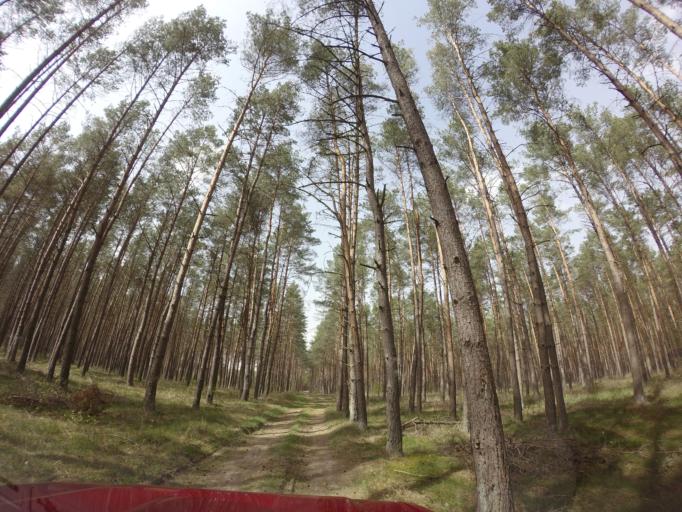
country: PL
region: West Pomeranian Voivodeship
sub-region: Powiat choszczenski
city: Drawno
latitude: 53.2687
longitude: 15.7135
